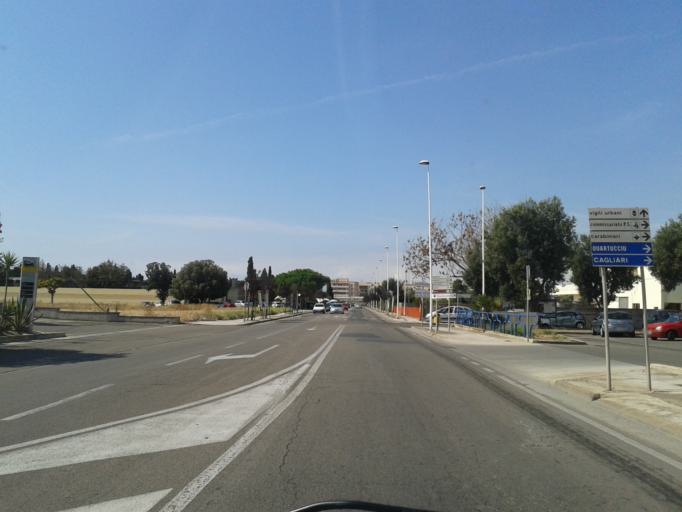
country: IT
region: Sardinia
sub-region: Provincia di Cagliari
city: Quartucciu
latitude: 39.2478
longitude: 9.1956
